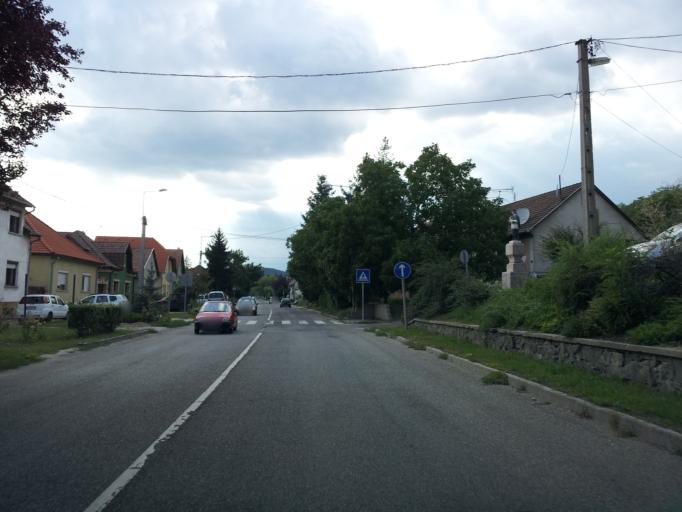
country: HU
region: Pest
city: Kismaros
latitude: 47.8267
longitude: 19.0071
